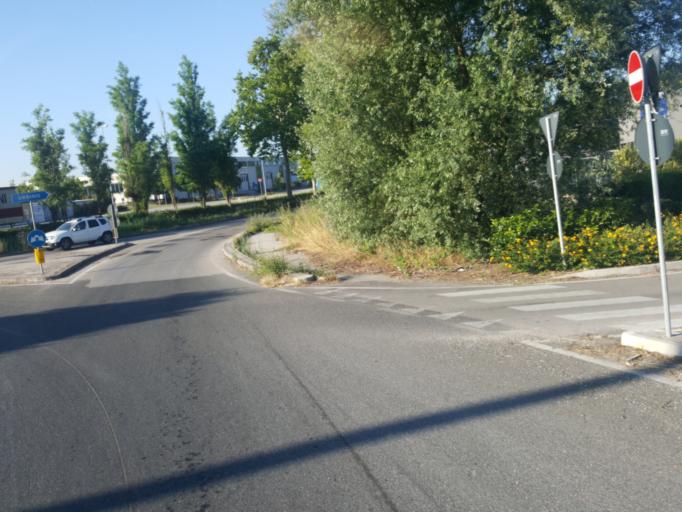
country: IT
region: The Marches
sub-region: Provincia di Pesaro e Urbino
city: Villa Ceccolini
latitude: 43.8911
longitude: 12.8331
